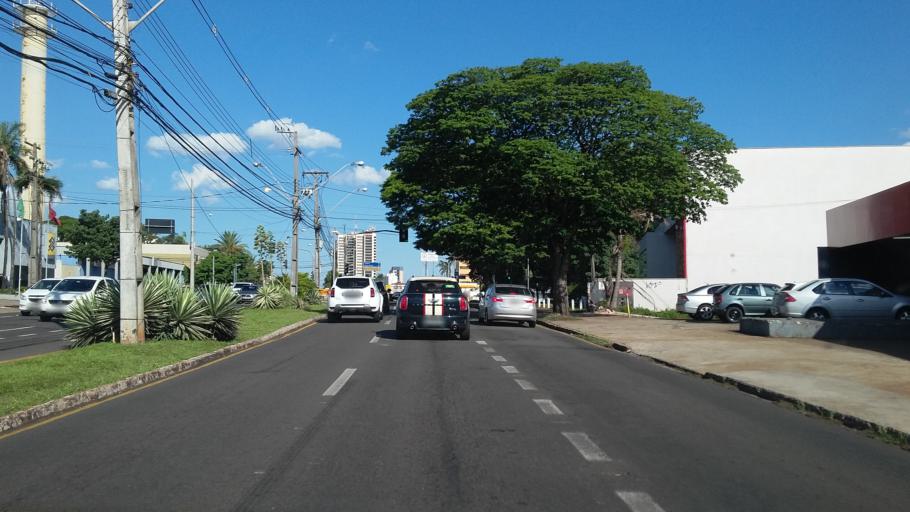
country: BR
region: Parana
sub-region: Londrina
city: Londrina
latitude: -23.3002
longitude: -51.1879
